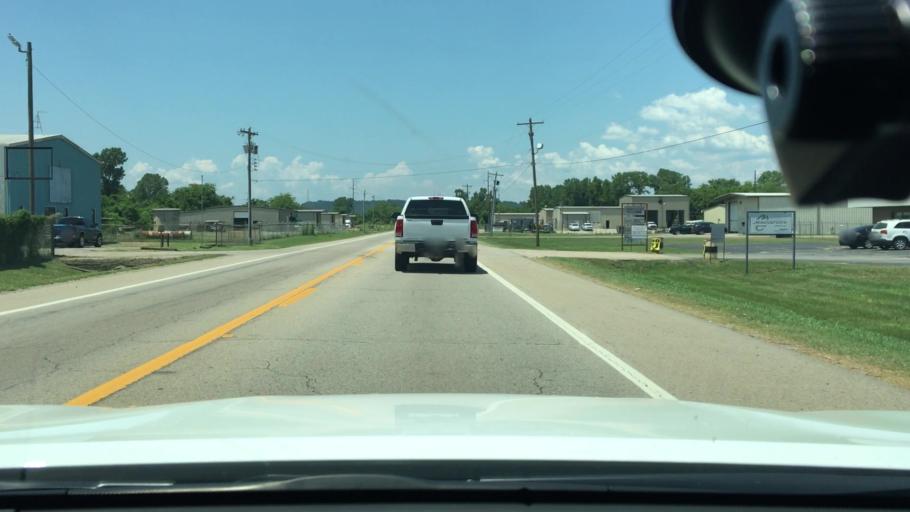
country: US
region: Arkansas
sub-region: Crawford County
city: Van Buren
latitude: 35.4158
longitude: -94.3322
